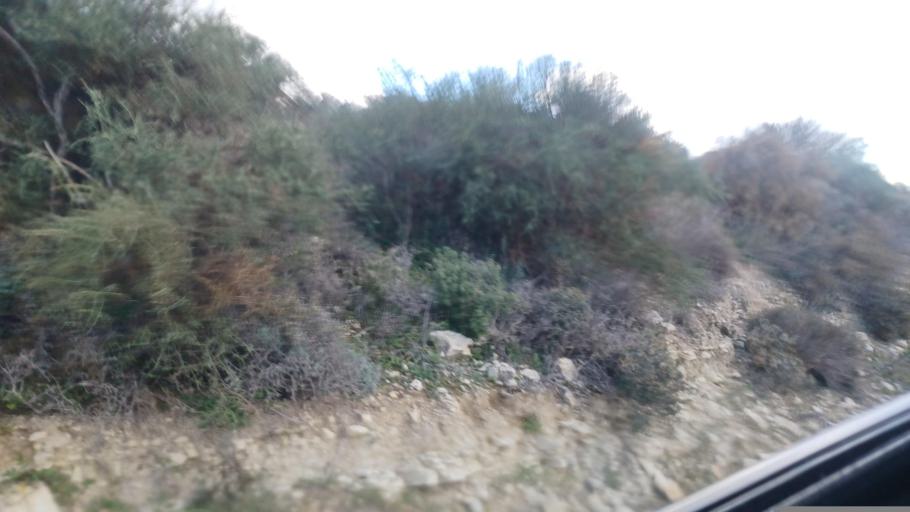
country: CY
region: Limassol
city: Pano Polemidia
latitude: 34.7703
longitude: 32.9794
